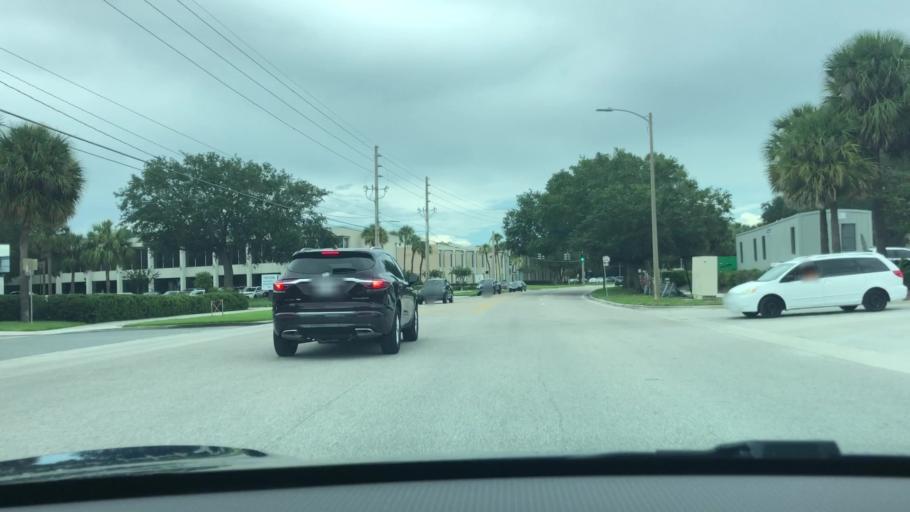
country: US
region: Florida
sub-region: Orange County
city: Orlando
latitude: 28.5556
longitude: -81.3440
